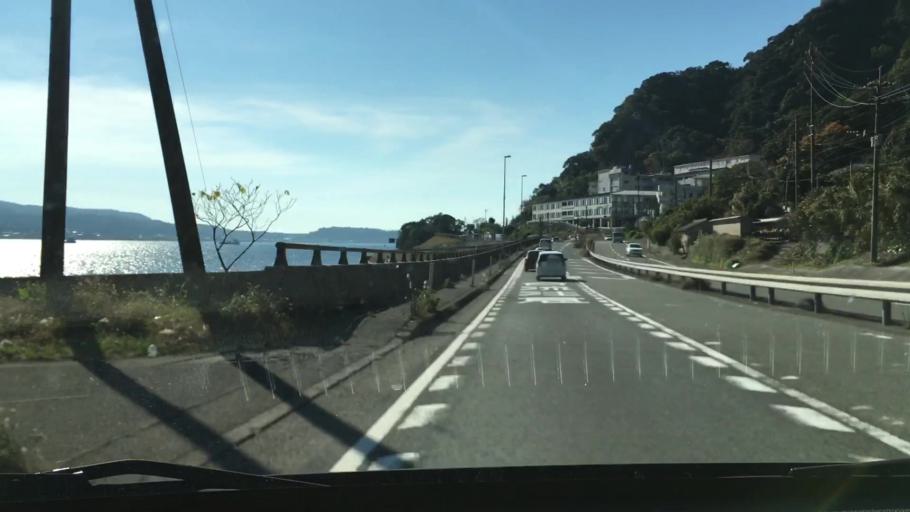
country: JP
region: Kagoshima
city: Kagoshima-shi
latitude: 31.6363
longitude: 130.6023
